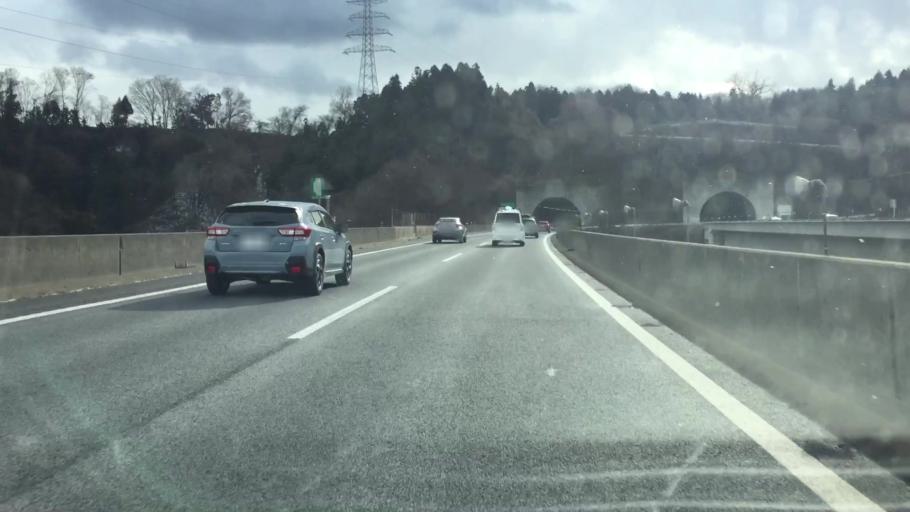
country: JP
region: Gunma
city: Numata
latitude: 36.5879
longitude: 139.0669
